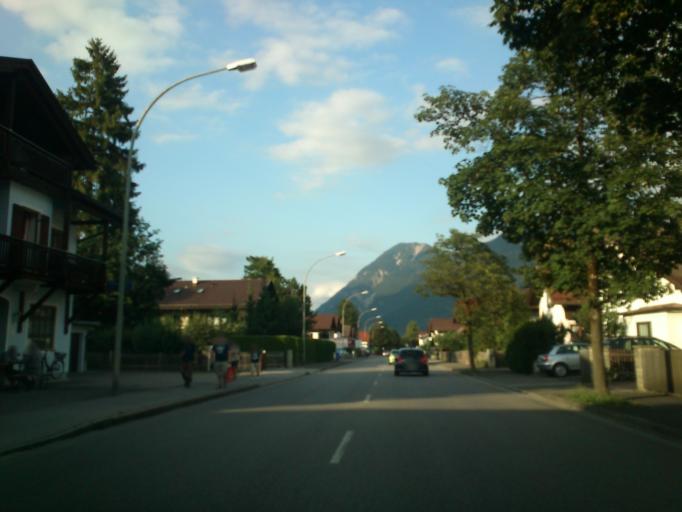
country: DE
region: Bavaria
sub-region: Upper Bavaria
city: Garmisch-Partenkirchen
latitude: 47.4875
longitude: 11.0708
